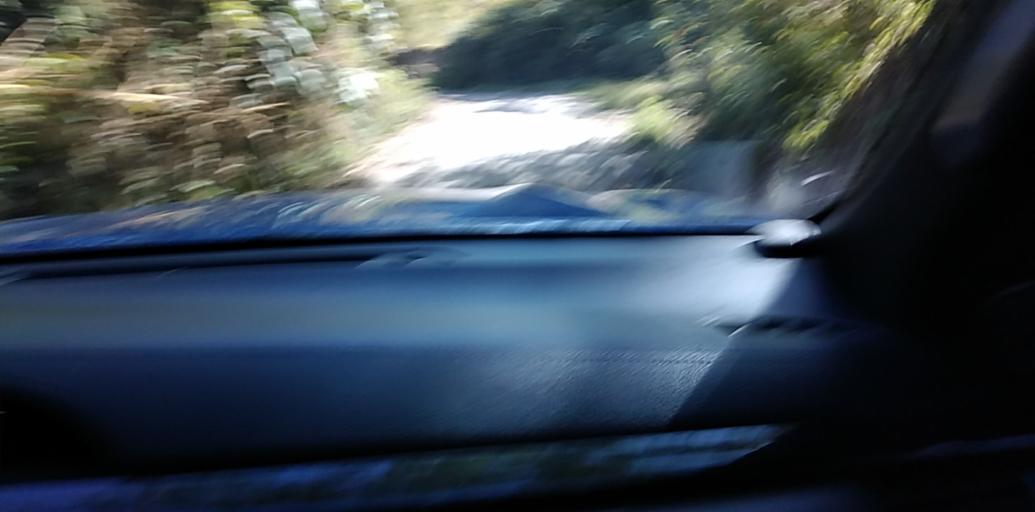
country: PH
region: Central Luzon
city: Santol
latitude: 15.1715
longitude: 120.4749
